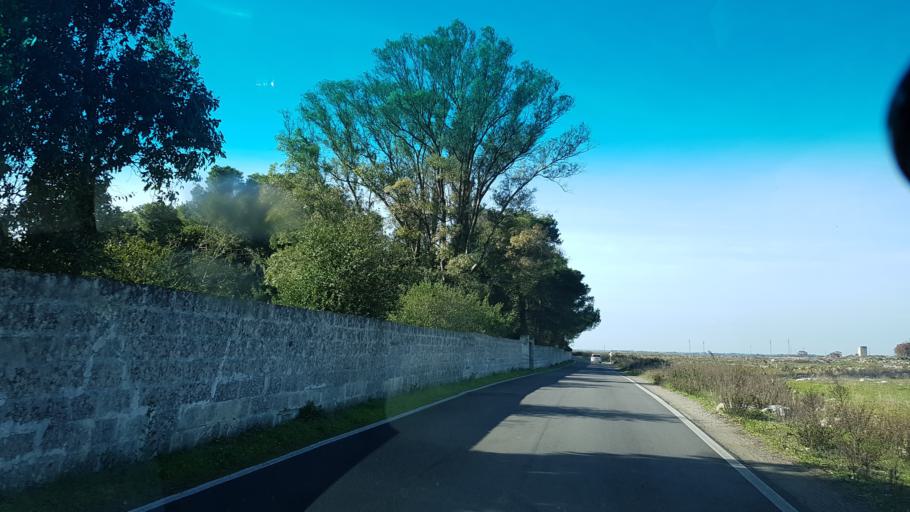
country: IT
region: Apulia
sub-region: Provincia di Lecce
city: Lecce
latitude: 40.3495
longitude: 18.1425
